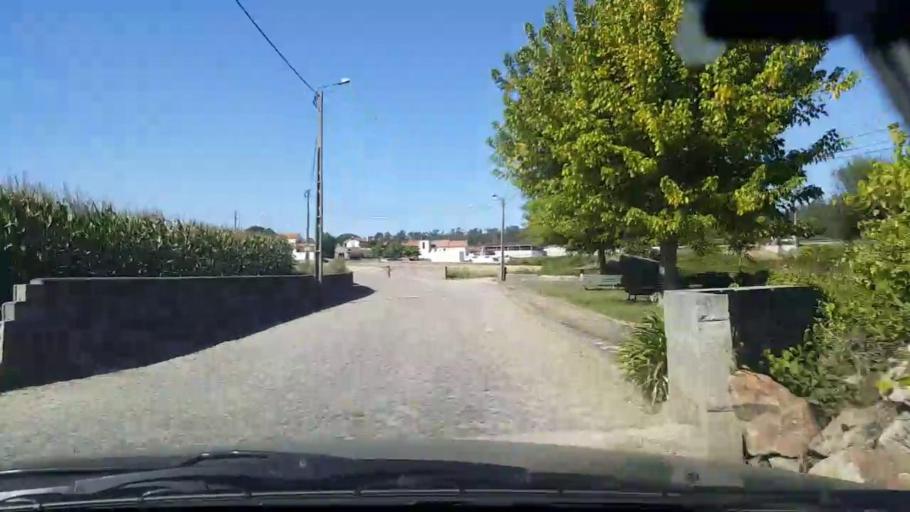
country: PT
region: Braga
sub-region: Vila Nova de Famalicao
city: Ribeirao
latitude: 41.3588
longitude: -8.6353
